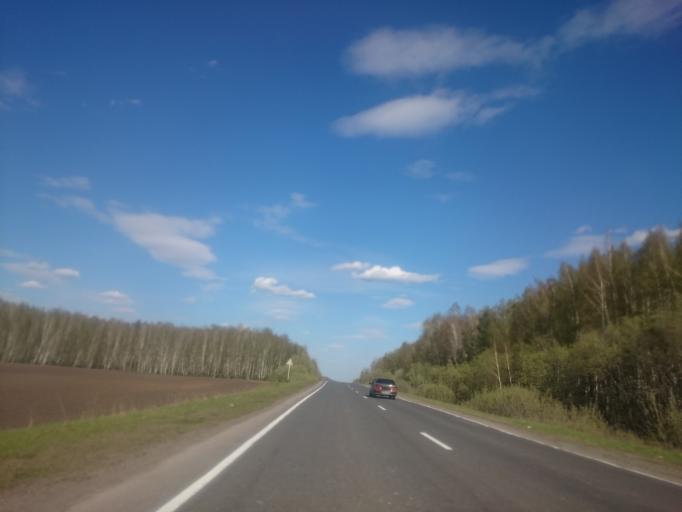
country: RU
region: Sverdlovsk
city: Lesnoy
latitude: 57.6182
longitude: 63.1881
